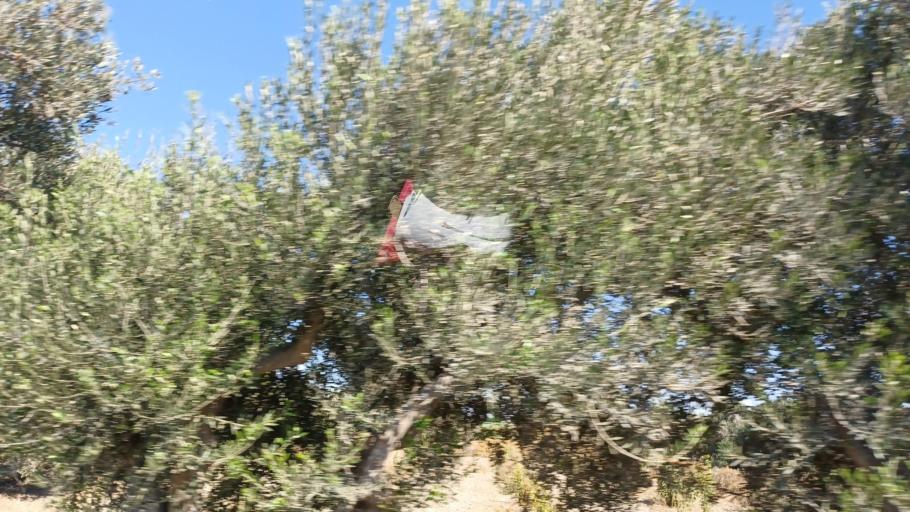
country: CY
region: Larnaka
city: Kolossi
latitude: 34.6360
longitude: 32.9252
